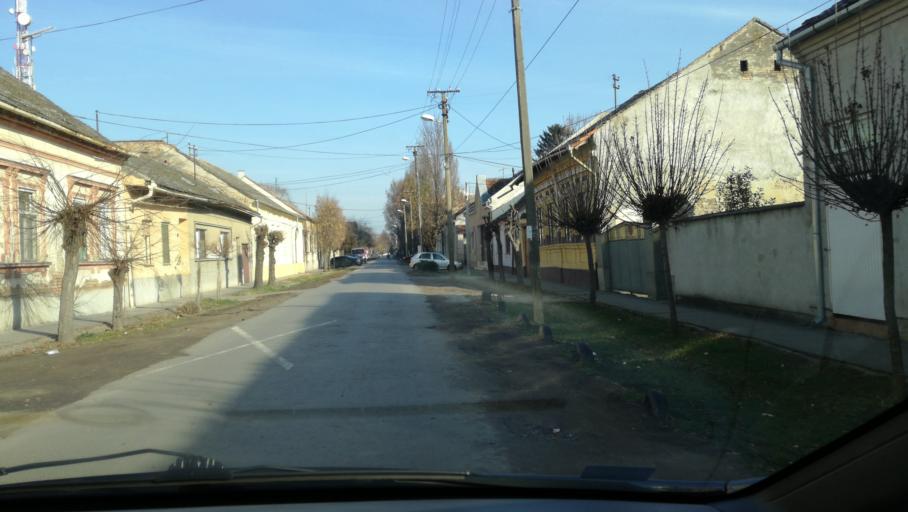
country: RS
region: Autonomna Pokrajina Vojvodina
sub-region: Severnobanatski Okrug
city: Kikinda
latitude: 45.8282
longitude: 20.4671
